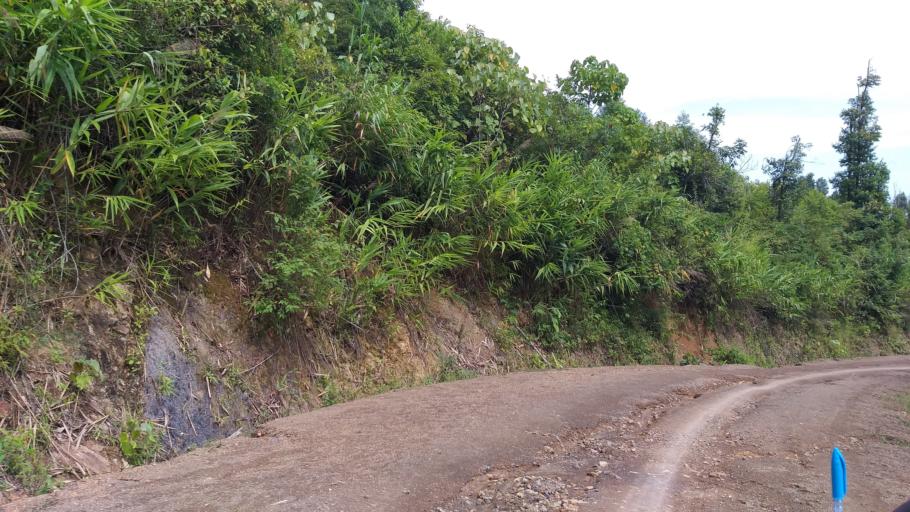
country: VN
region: Huyen Dien Bien
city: Dien Bien Phu
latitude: 21.4760
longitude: 102.6813
